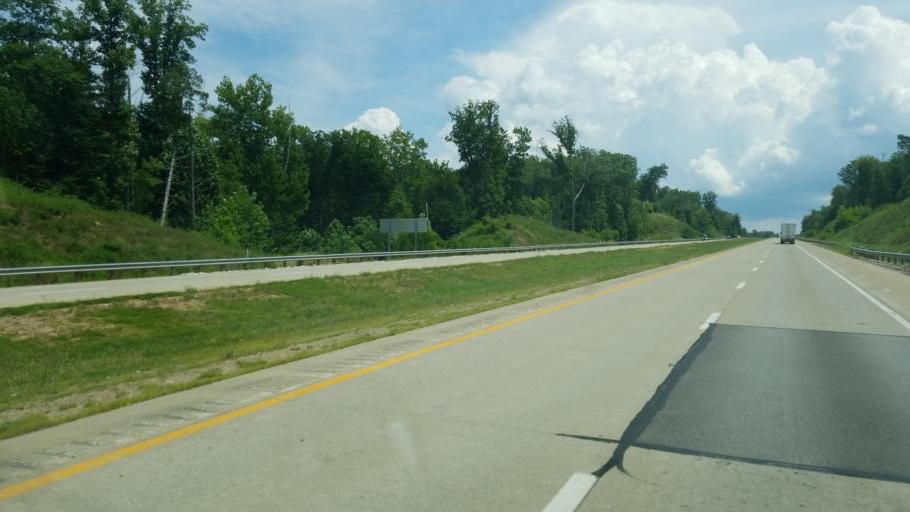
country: US
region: West Virginia
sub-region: Putnam County
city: Eleanor
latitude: 38.5451
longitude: -81.9726
